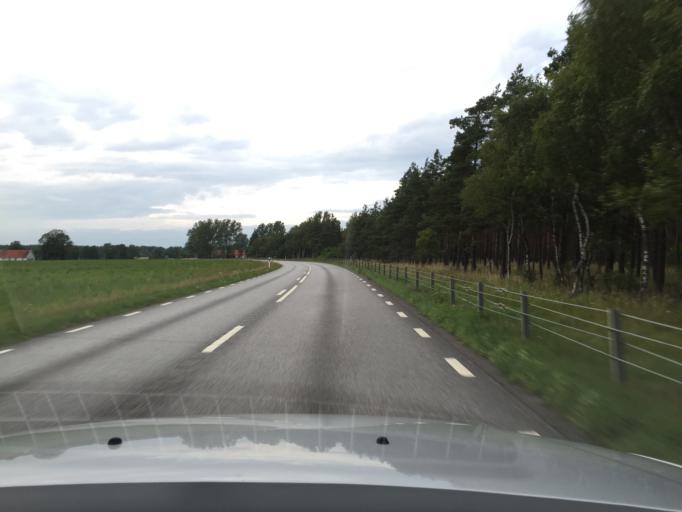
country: SE
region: Skane
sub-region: Kristianstads Kommun
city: Norra Asum
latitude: 55.9319
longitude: 14.0753
